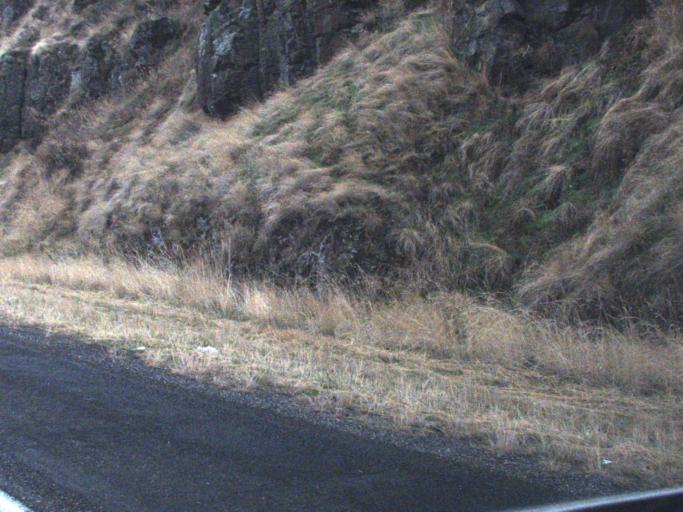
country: US
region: Washington
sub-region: Asotin County
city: Clarkston Heights-Vineland
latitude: 46.4241
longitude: -117.1275
